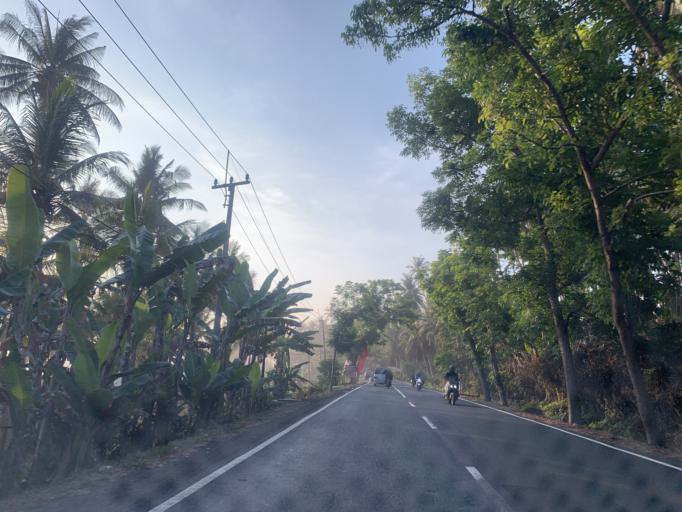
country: ID
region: Bali
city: Banjar Swastika
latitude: -8.4639
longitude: 114.9119
